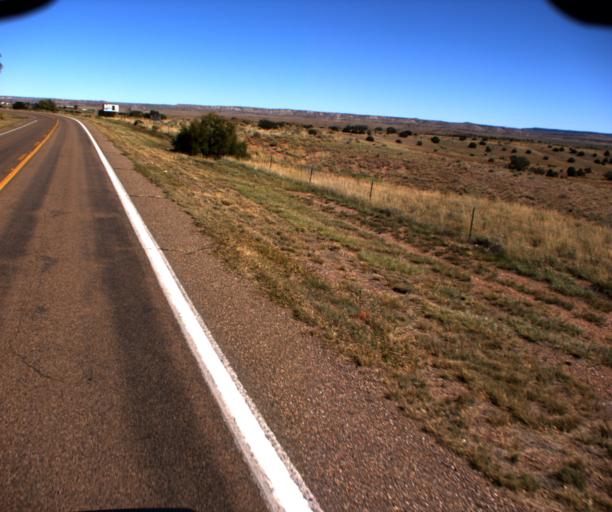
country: US
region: Arizona
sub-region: Apache County
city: Saint Johns
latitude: 34.4903
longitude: -109.3733
